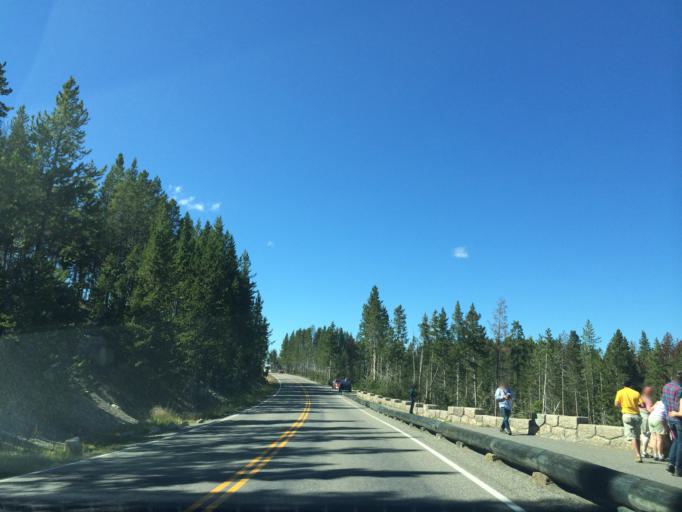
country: US
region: Montana
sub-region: Gallatin County
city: West Yellowstone
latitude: 44.6278
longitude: -110.4332
